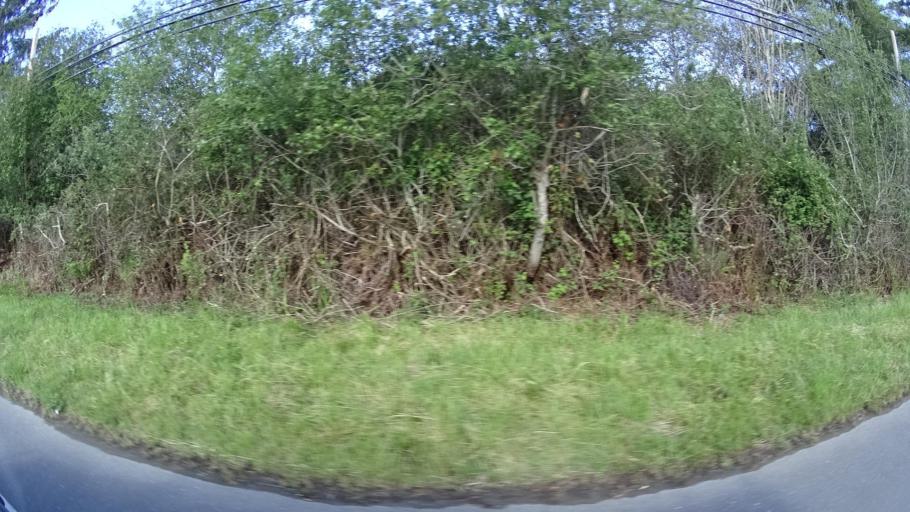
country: US
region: California
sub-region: Humboldt County
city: McKinleyville
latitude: 40.9592
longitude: -124.1009
